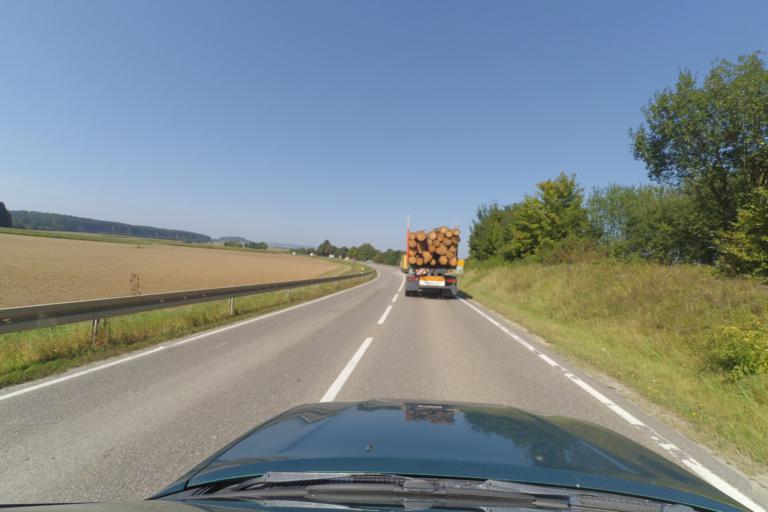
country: DE
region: Bavaria
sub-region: Swabia
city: Wittislingen
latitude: 48.6202
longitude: 10.4053
